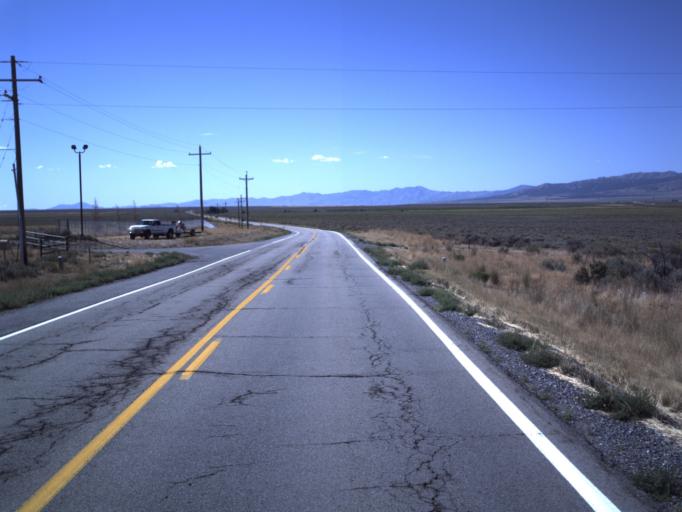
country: US
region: Utah
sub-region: Tooele County
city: Tooele
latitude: 40.4073
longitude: -112.3852
